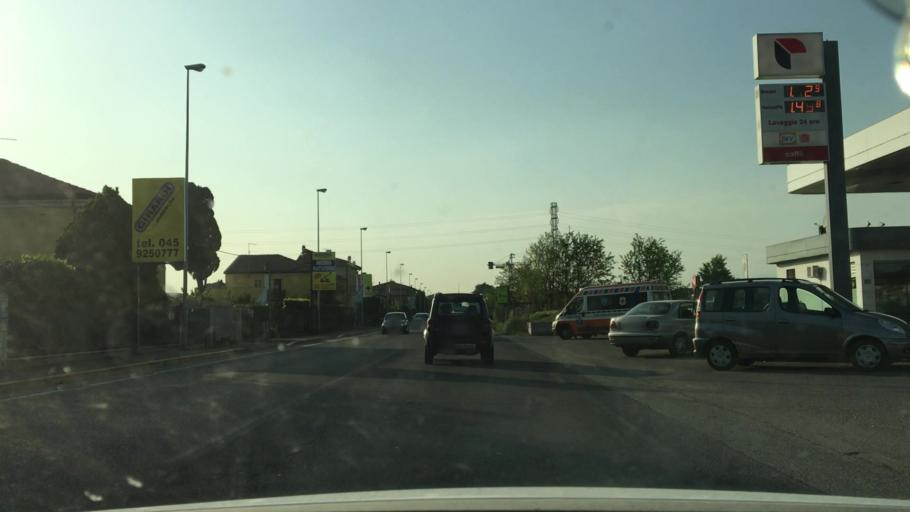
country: IT
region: Veneto
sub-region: Provincia di Verona
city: San Giovanni Lupatoto
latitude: 45.4052
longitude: 11.0115
